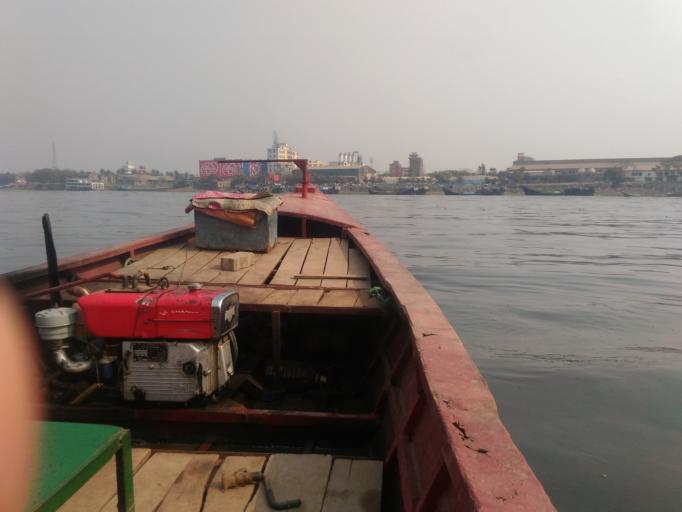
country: BD
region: Dhaka
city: Narayanganj
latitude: 23.6337
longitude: 90.4599
